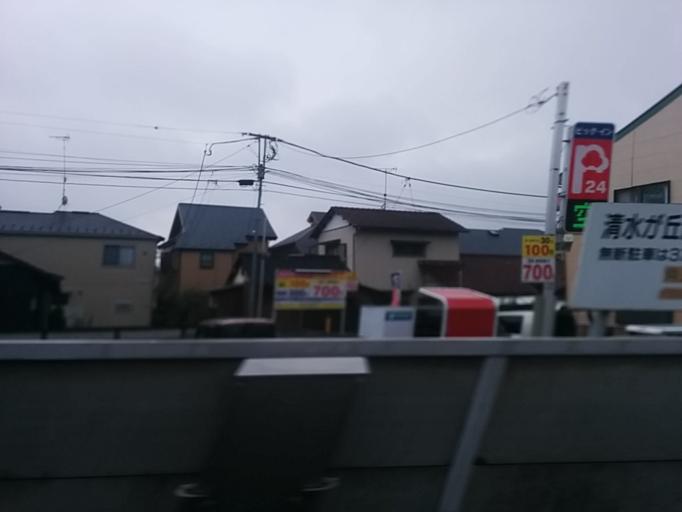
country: JP
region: Tokyo
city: Kokubunji
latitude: 35.6682
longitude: 139.4973
